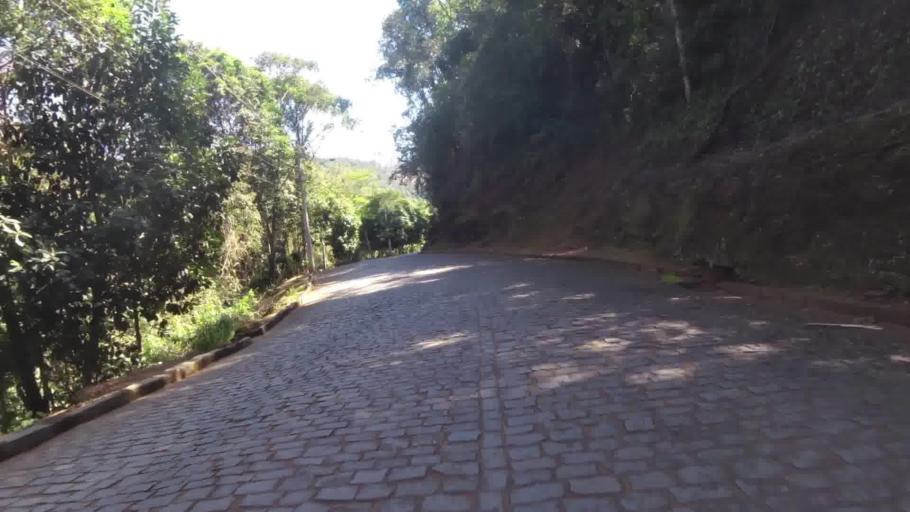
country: BR
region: Espirito Santo
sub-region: Alfredo Chaves
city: Alfredo Chaves
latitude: -20.5559
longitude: -40.8183
